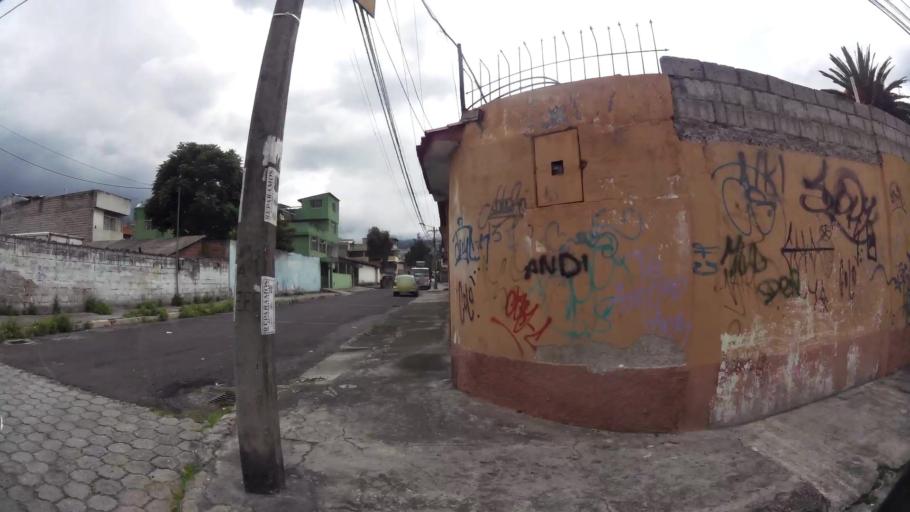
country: EC
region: Pichincha
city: Quito
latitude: -0.2479
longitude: -78.5282
